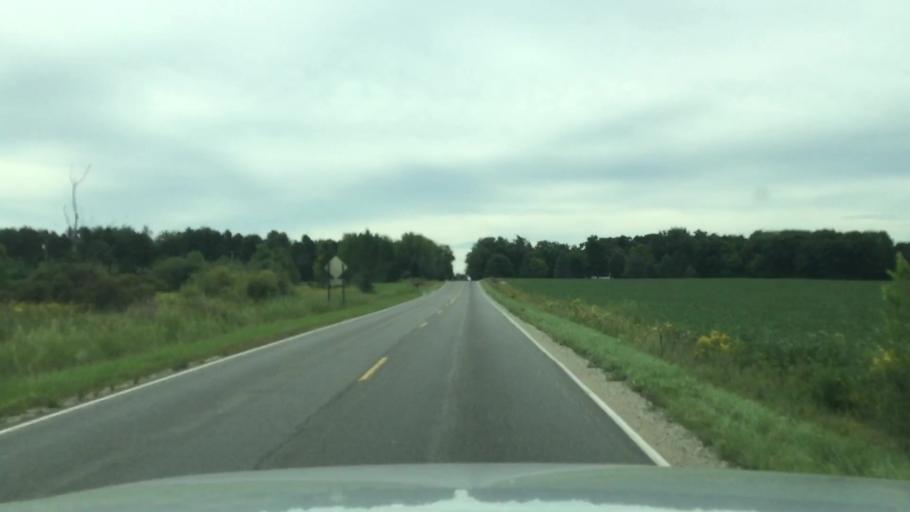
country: US
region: Michigan
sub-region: Shiawassee County
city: Durand
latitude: 42.9697
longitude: -83.9868
